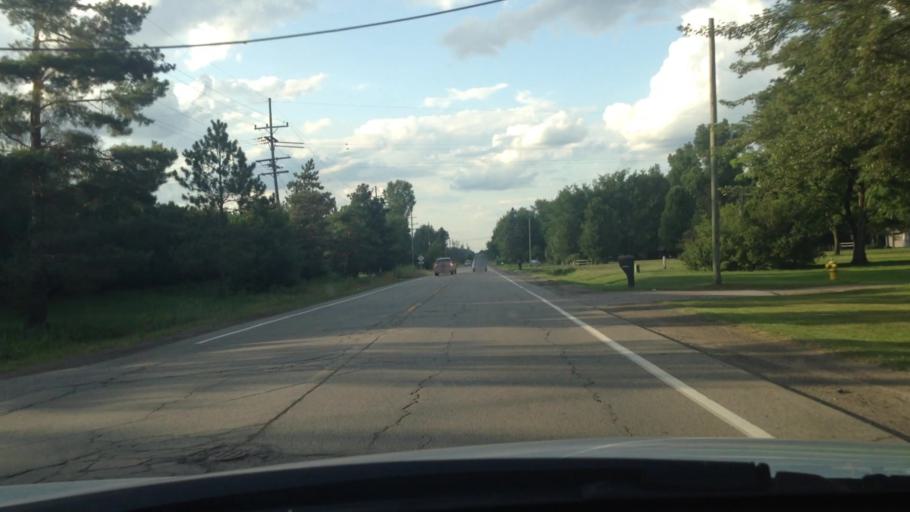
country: US
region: Michigan
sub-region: Wayne County
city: Flat Rock
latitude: 42.1594
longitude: -83.3055
